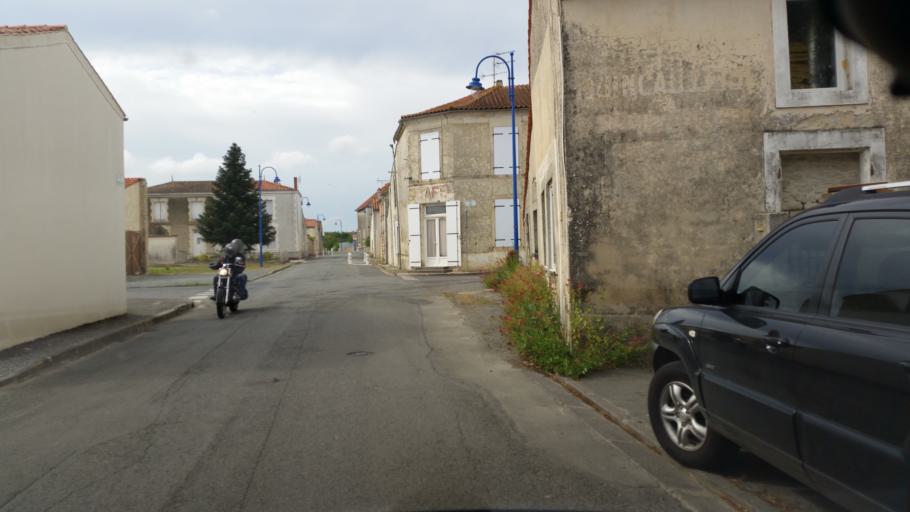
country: FR
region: Poitou-Charentes
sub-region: Departement de la Charente-Maritime
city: Courcon
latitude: 46.1891
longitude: -0.8633
